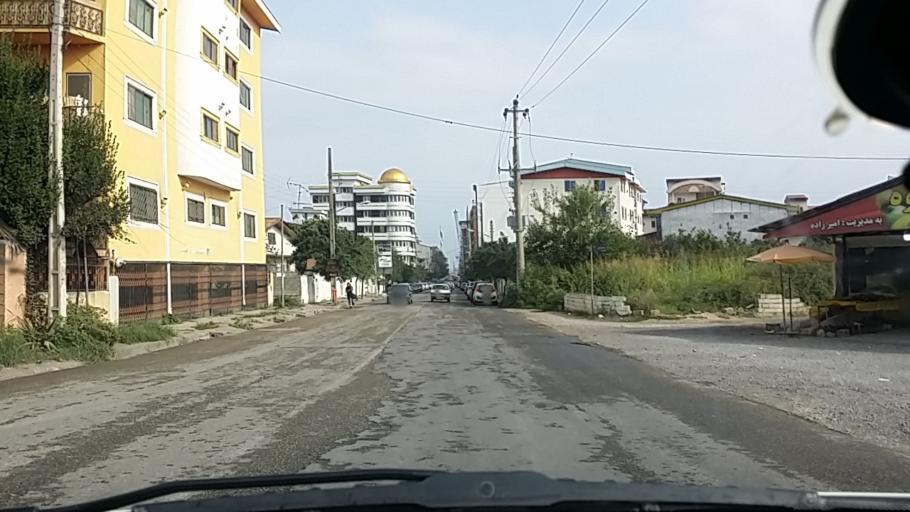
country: IR
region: Mazandaran
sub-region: Nowshahr
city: Nowshahr
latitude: 36.6473
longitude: 51.5085
